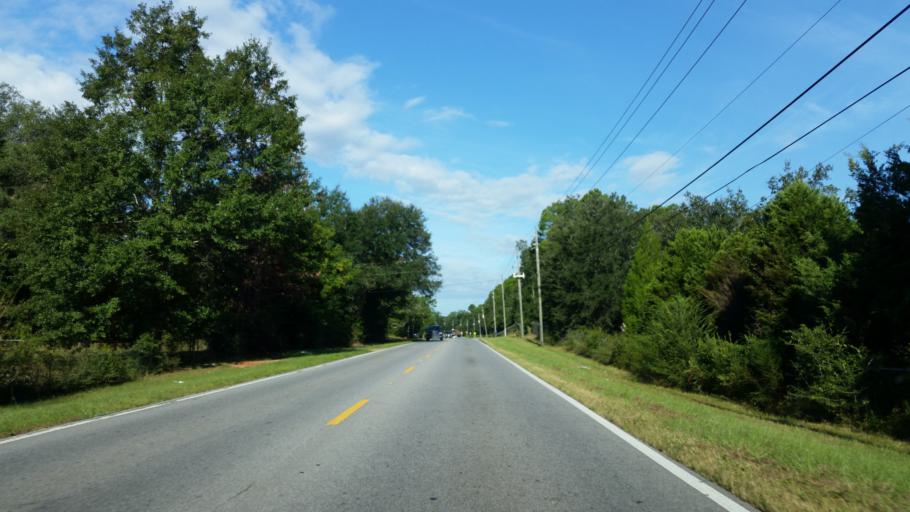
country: US
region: Florida
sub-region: Santa Rosa County
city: Milton
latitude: 30.6397
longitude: -87.0868
